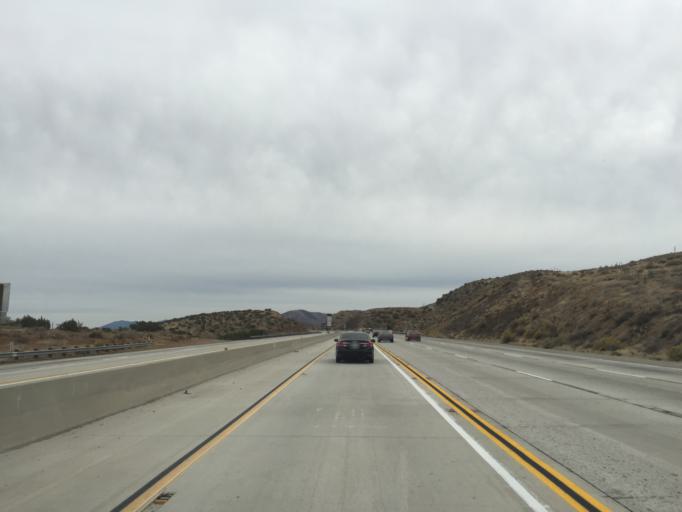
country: US
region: California
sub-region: Los Angeles County
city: Vincent
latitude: 34.5385
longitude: -118.1211
